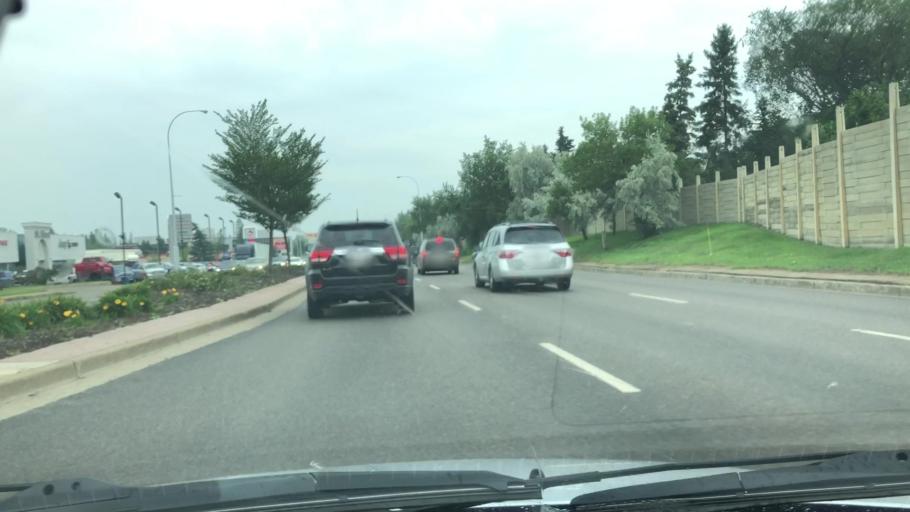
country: CA
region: Alberta
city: St. Albert
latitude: 53.6238
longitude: -113.6133
